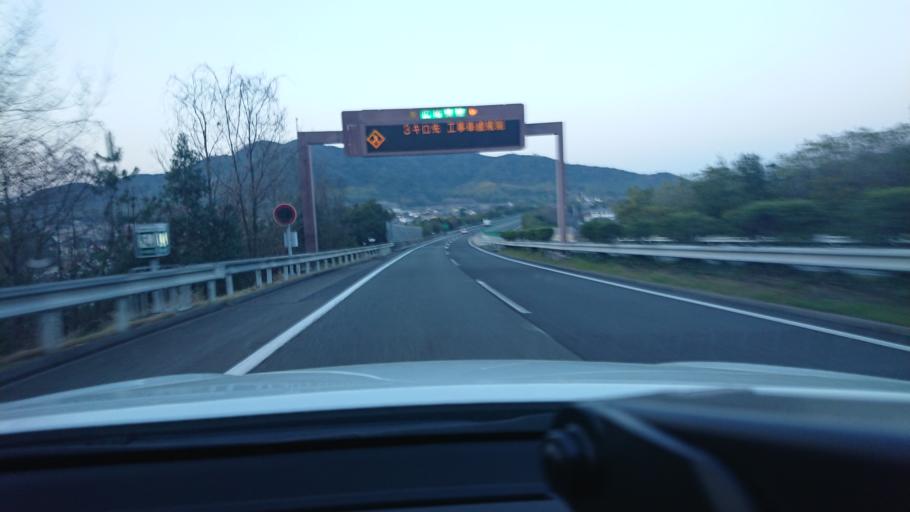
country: JP
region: Kagawa
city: Takamatsu-shi
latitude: 34.2813
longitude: 133.9673
